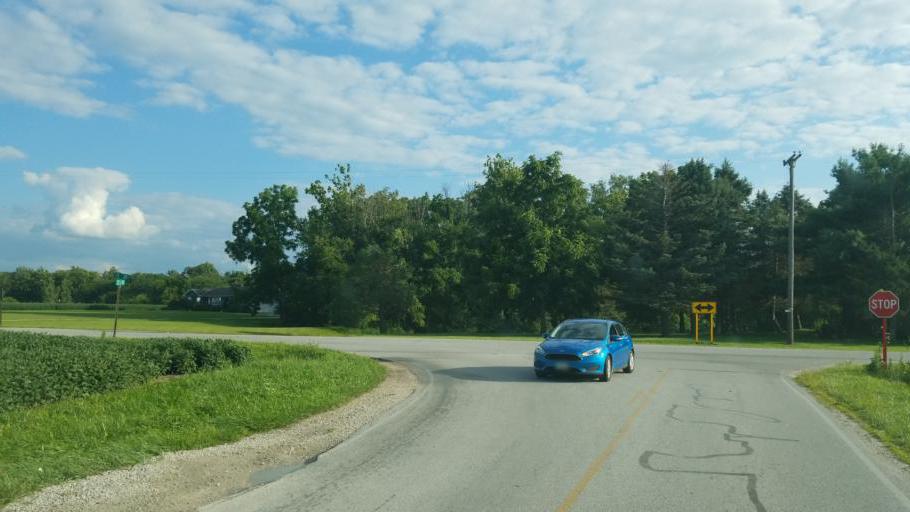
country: US
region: Ohio
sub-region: Seneca County
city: Tiffin
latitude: 41.1679
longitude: -83.1244
